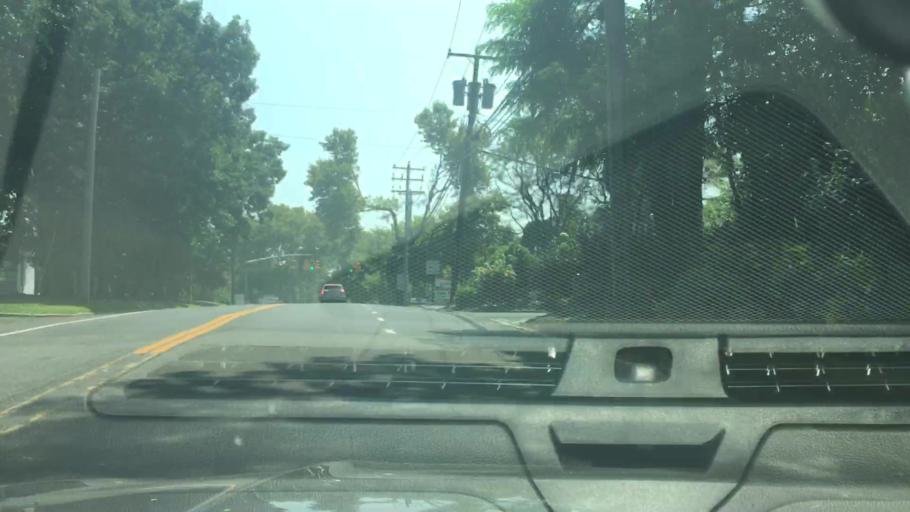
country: US
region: New York
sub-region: Suffolk County
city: Hauppauge
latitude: 40.8170
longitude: -73.2334
